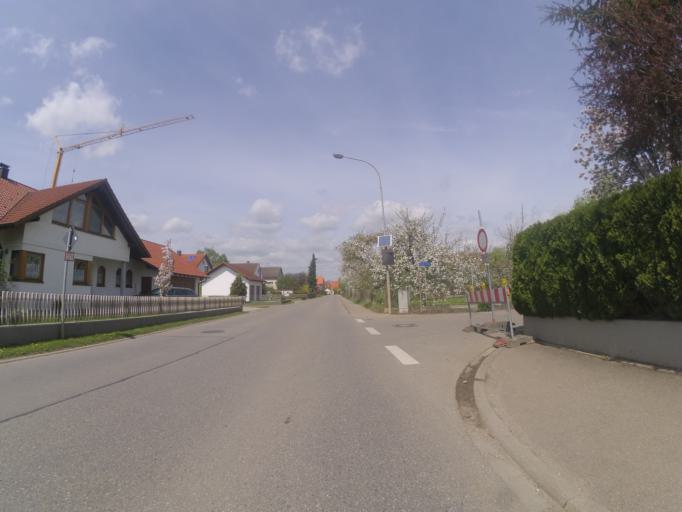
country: DE
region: Baden-Wuerttemberg
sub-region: Tuebingen Region
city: Ersingen
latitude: 48.2887
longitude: 9.8530
